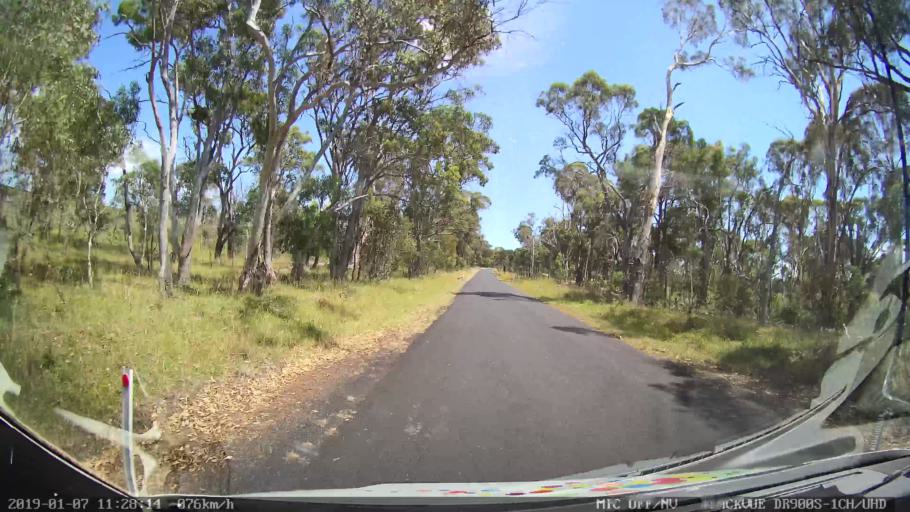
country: AU
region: New South Wales
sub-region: Armidale Dumaresq
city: Armidale
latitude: -30.4506
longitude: 151.5675
